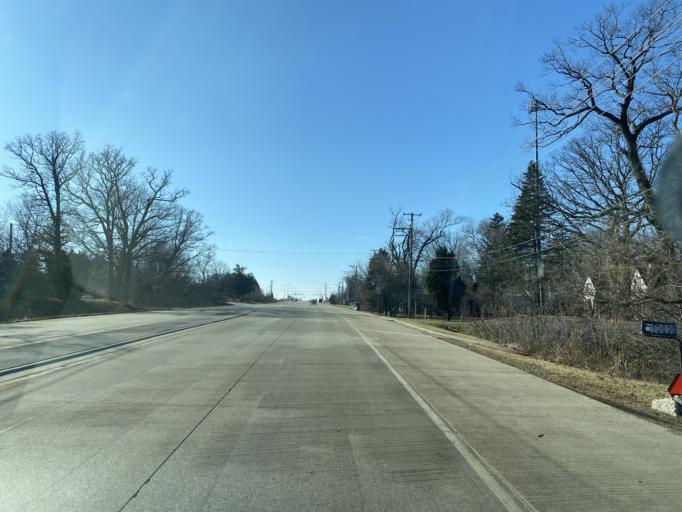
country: US
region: Illinois
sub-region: Cook County
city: Lemont
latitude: 41.6392
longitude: -88.0063
